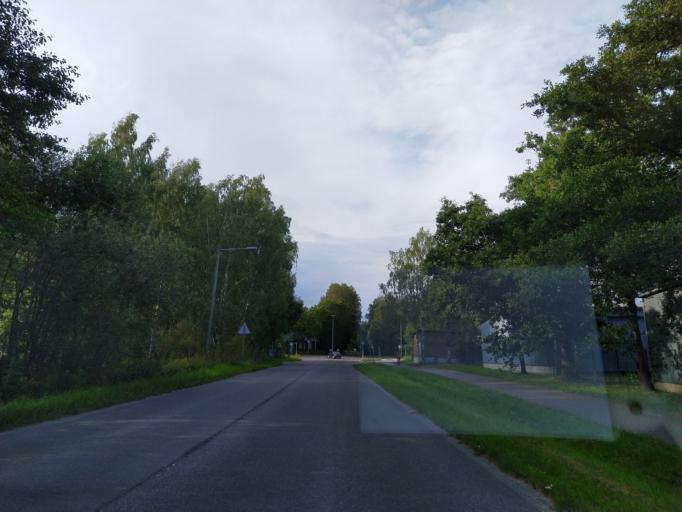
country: FI
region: Varsinais-Suomi
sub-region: Turku
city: Turku
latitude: 60.4261
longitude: 22.2266
